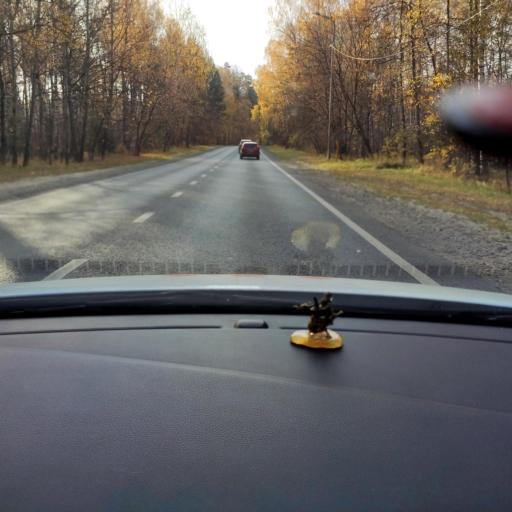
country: RU
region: Tatarstan
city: Osinovo
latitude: 55.8347
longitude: 48.8928
